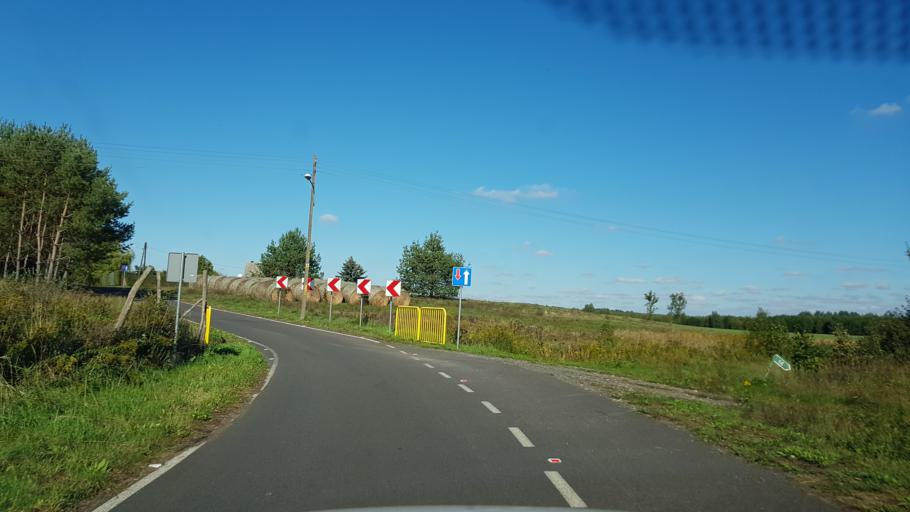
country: PL
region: Lubusz
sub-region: Powiat gorzowski
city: Lubiszyn
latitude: 52.8578
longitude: 14.9683
